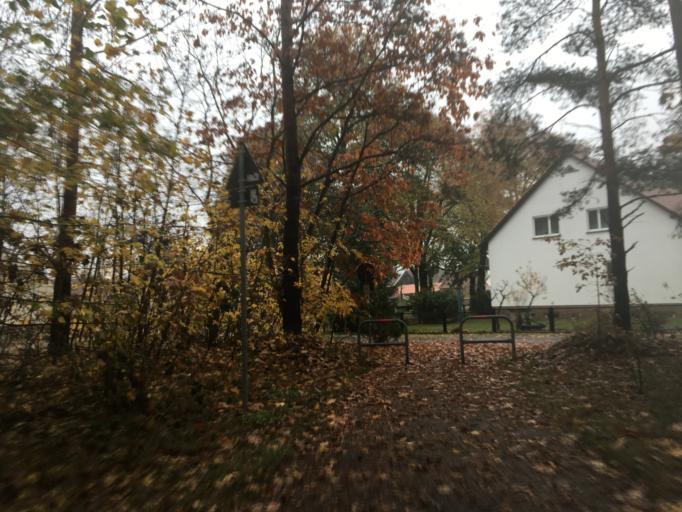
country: DE
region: Brandenburg
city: Schlepzig
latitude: 52.0322
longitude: 13.8188
